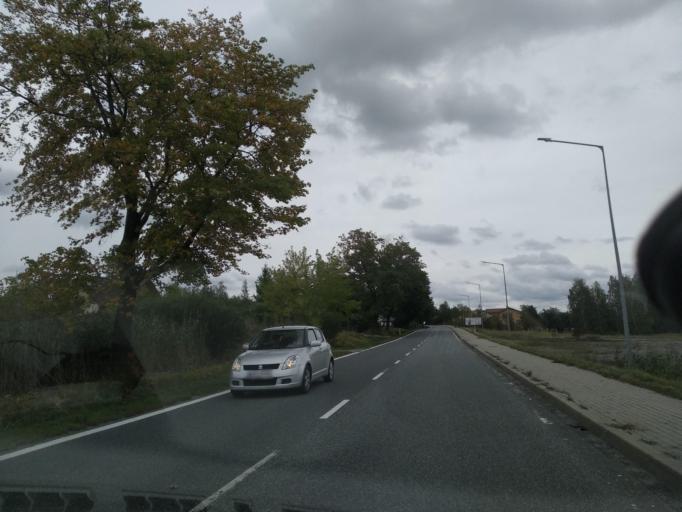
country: PL
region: Subcarpathian Voivodeship
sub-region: Powiat krosnienski
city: Dukla
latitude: 49.5578
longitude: 21.6422
